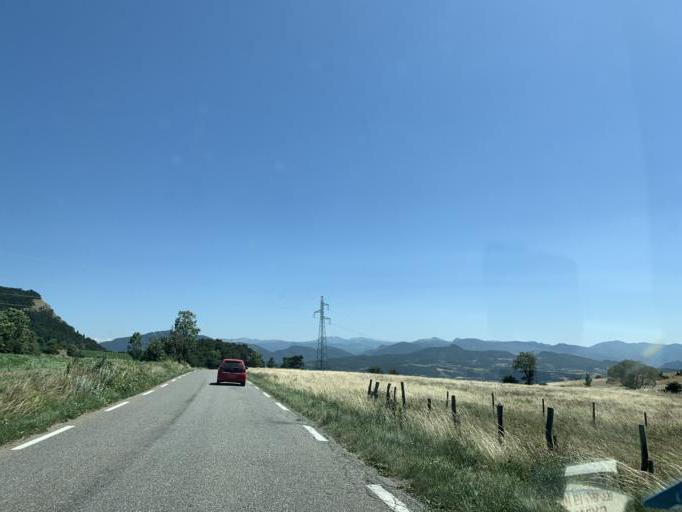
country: FR
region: Provence-Alpes-Cote d'Azur
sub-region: Departement des Hautes-Alpes
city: Gap
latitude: 44.6082
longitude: 6.1411
